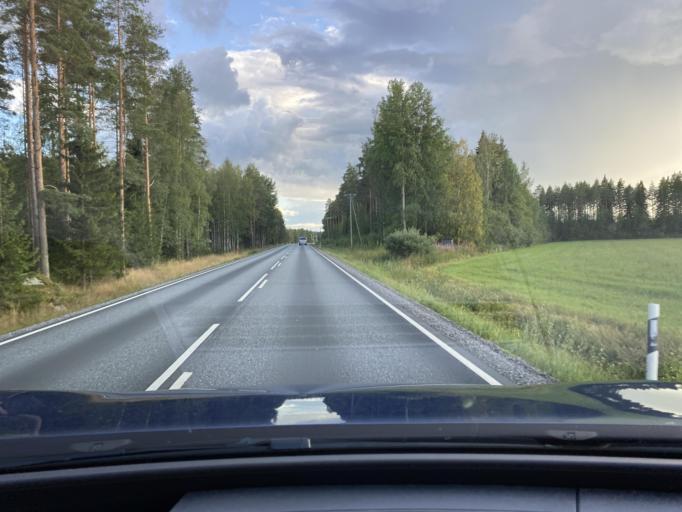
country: FI
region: Southern Ostrobothnia
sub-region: Seinaejoki
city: Jalasjaervi
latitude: 62.5165
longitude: 22.6594
